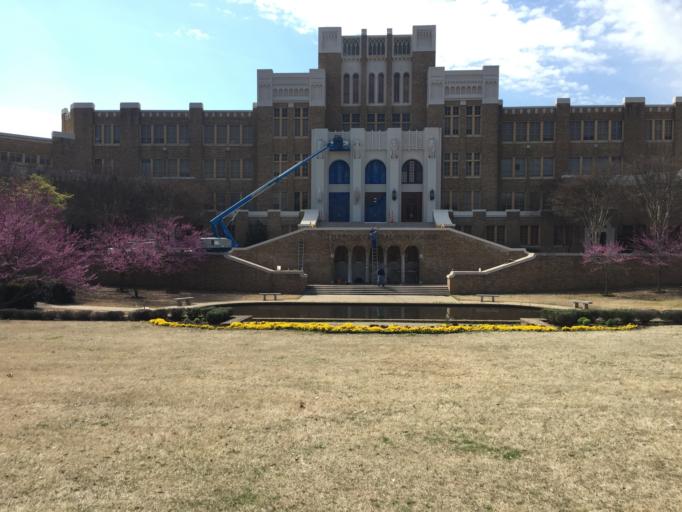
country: US
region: Arkansas
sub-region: Pulaski County
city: Little Rock
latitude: 34.7368
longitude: -92.2979
